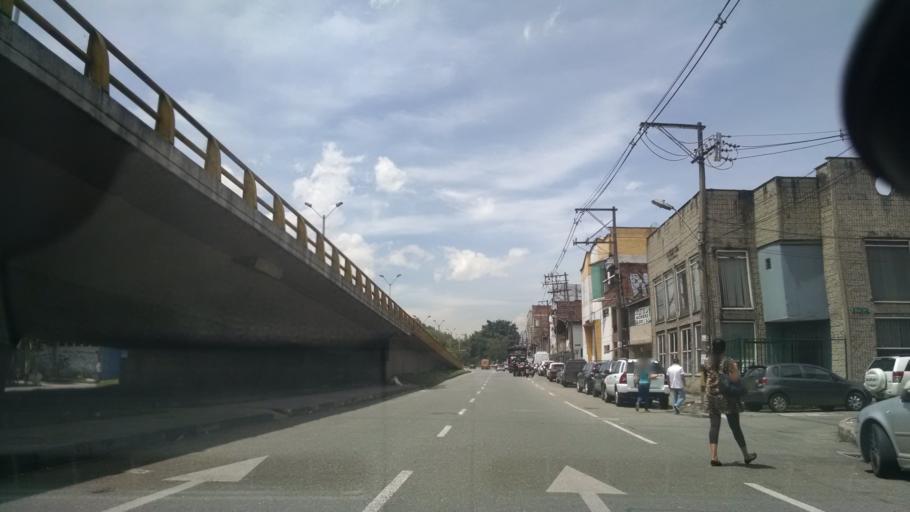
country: CO
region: Antioquia
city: Itagui
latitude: 6.2144
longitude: -75.5822
